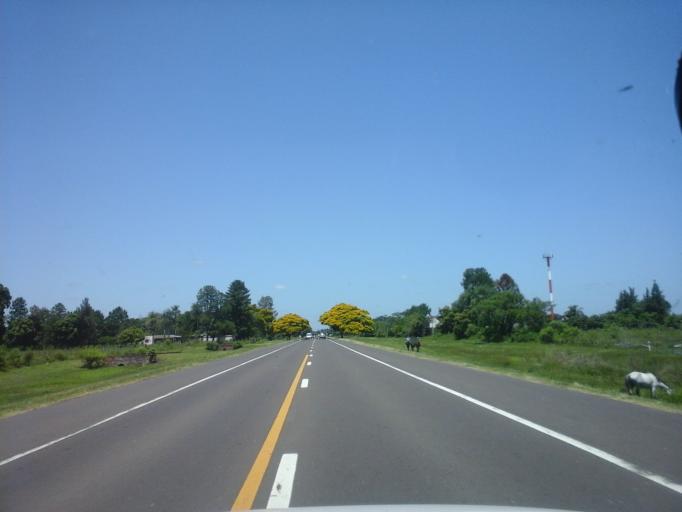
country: AR
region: Corrientes
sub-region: Departamento de San Cosme
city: San Cosme
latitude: -27.3769
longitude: -58.5016
